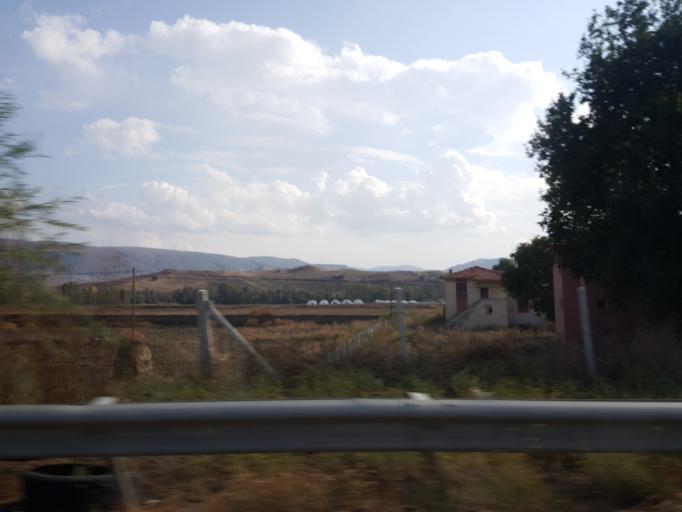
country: TR
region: Corum
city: Seydim
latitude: 40.4280
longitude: 34.7822
